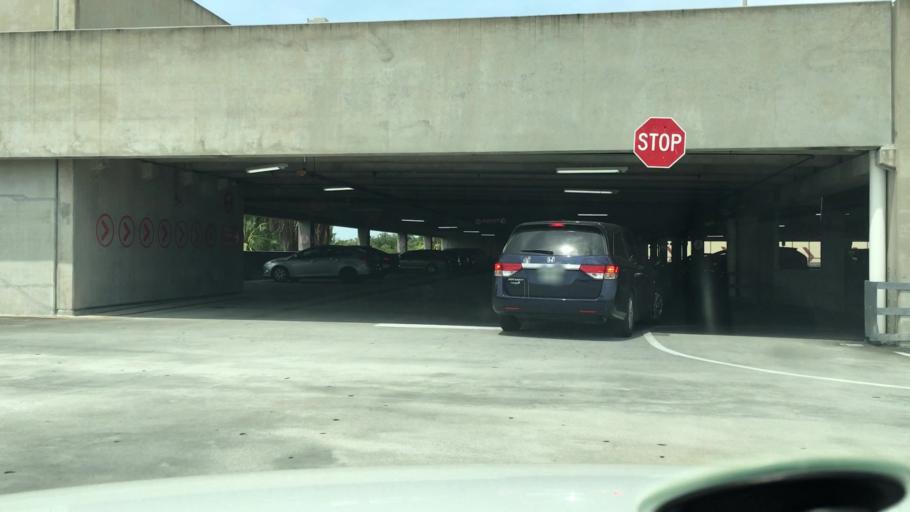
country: US
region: Florida
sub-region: Hillsborough County
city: Tampa
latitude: 27.9561
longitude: -82.5073
